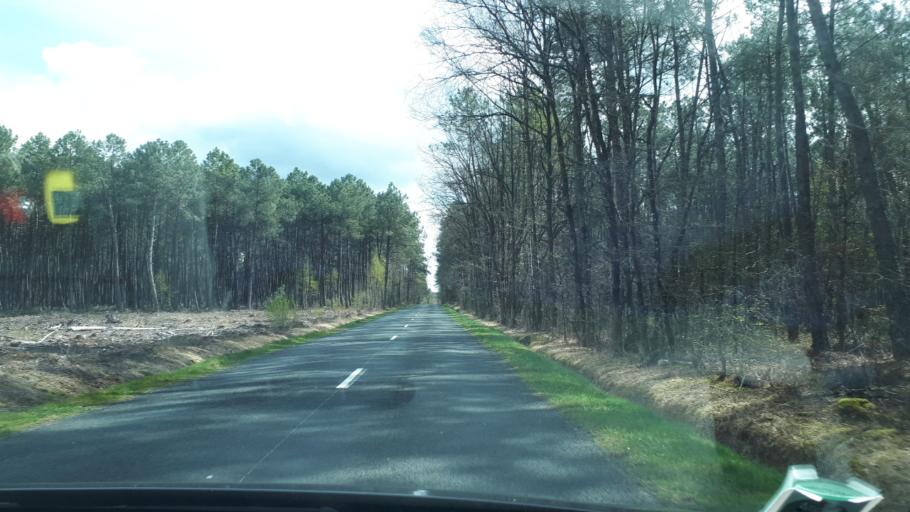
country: FR
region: Pays de la Loire
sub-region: Departement de la Sarthe
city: Brette-les-Pins
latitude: 47.8681
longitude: 0.3746
